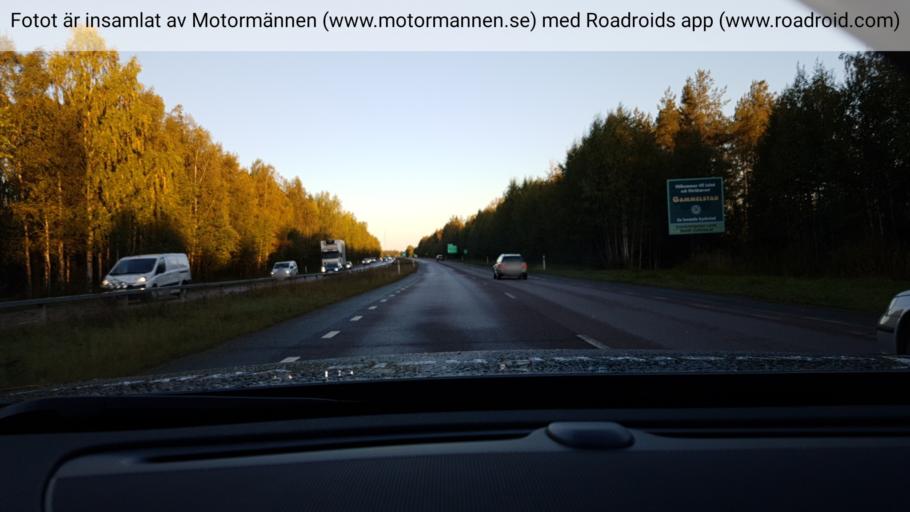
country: SE
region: Norrbotten
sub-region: Lulea Kommun
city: Bergnaset
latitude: 65.6172
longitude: 22.0925
